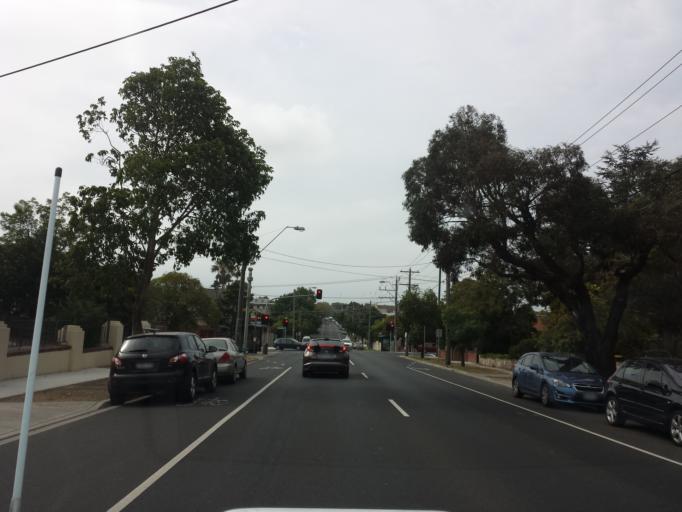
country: AU
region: Victoria
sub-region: Port Phillip
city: St Kilda East
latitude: -37.8683
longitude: 145.0090
